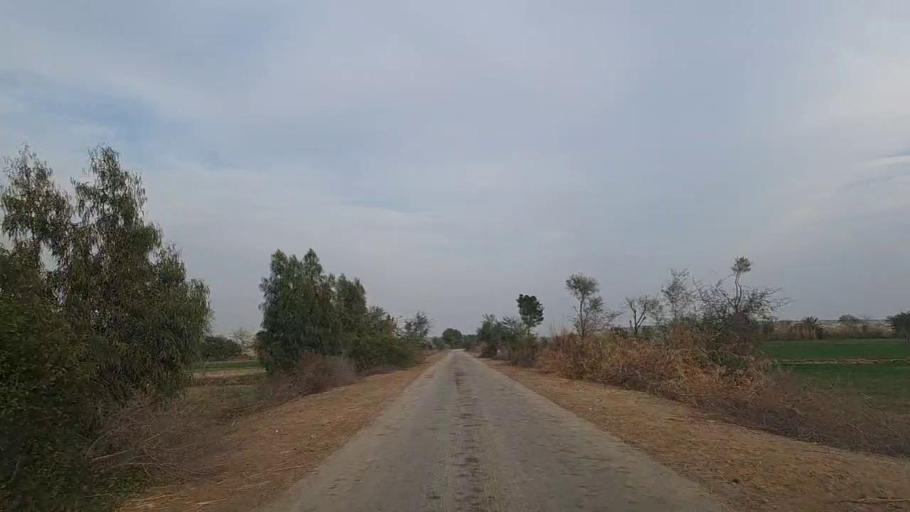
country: PK
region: Sindh
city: Daur
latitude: 26.5155
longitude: 68.4843
